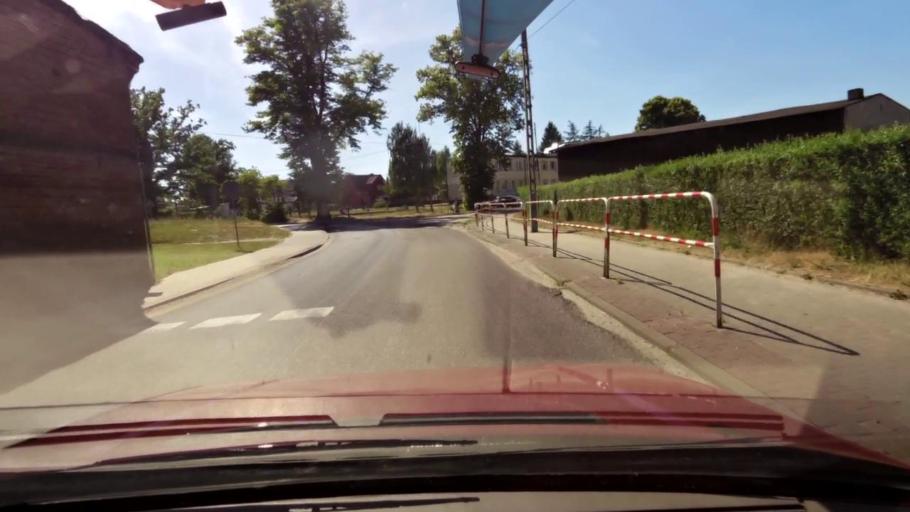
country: PL
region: Pomeranian Voivodeship
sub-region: Powiat slupski
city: Kobylnica
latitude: 54.3829
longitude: 16.9658
